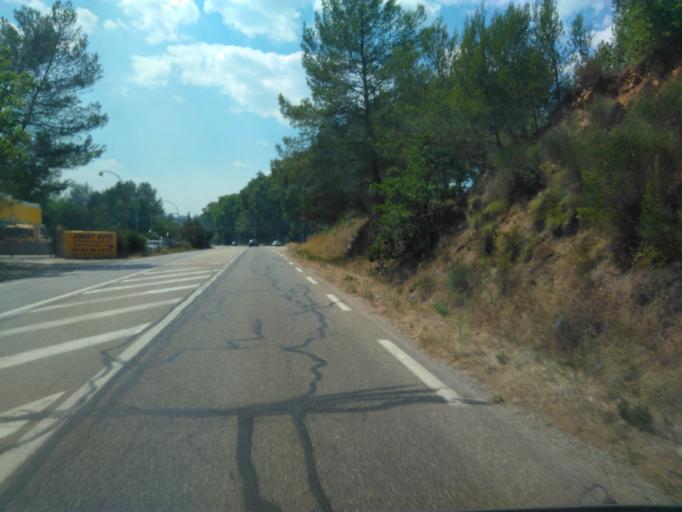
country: FR
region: Provence-Alpes-Cote d'Azur
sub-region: Departement du Var
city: Le Luc
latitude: 43.3964
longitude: 6.2959
